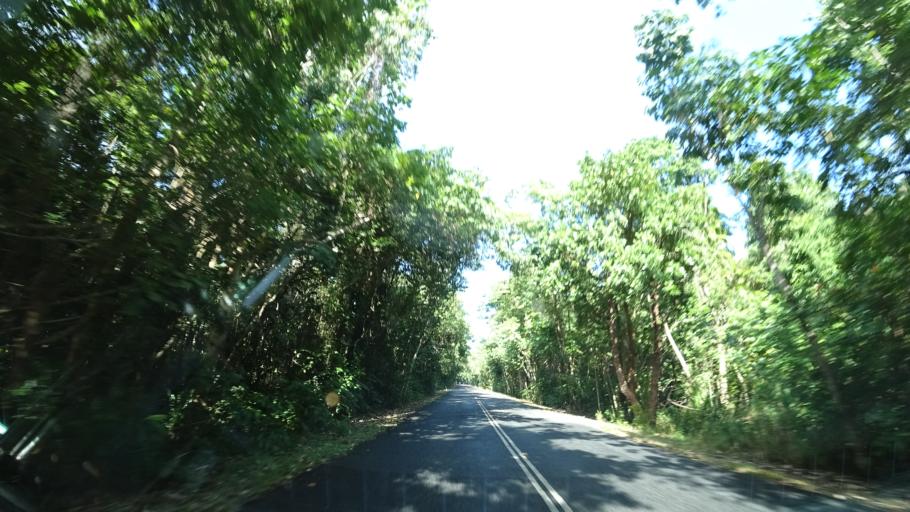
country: AU
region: Queensland
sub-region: Cairns
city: Port Douglas
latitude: -16.1321
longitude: 145.4523
